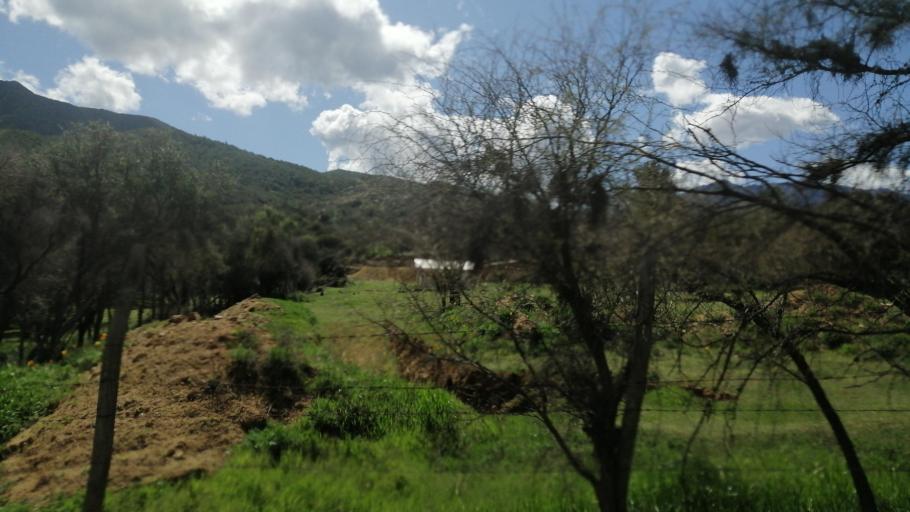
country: CL
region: Valparaiso
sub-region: Provincia de Marga Marga
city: Limache
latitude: -33.1879
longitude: -71.1937
